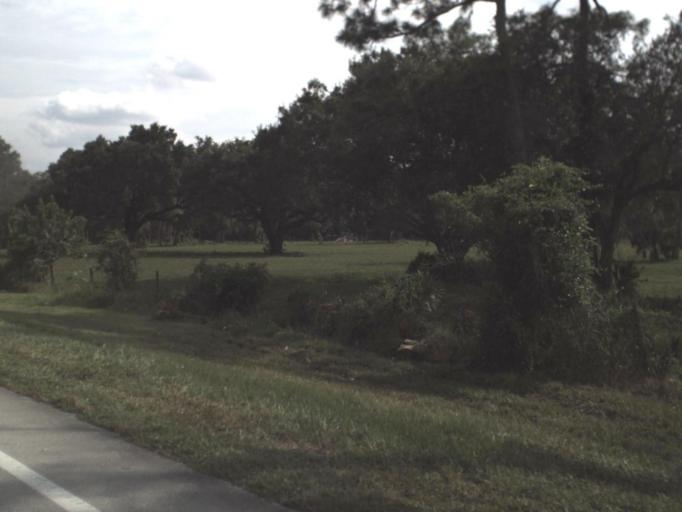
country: US
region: Florida
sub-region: Okeechobee County
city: Taylor Creek
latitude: 27.2349
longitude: -80.7779
